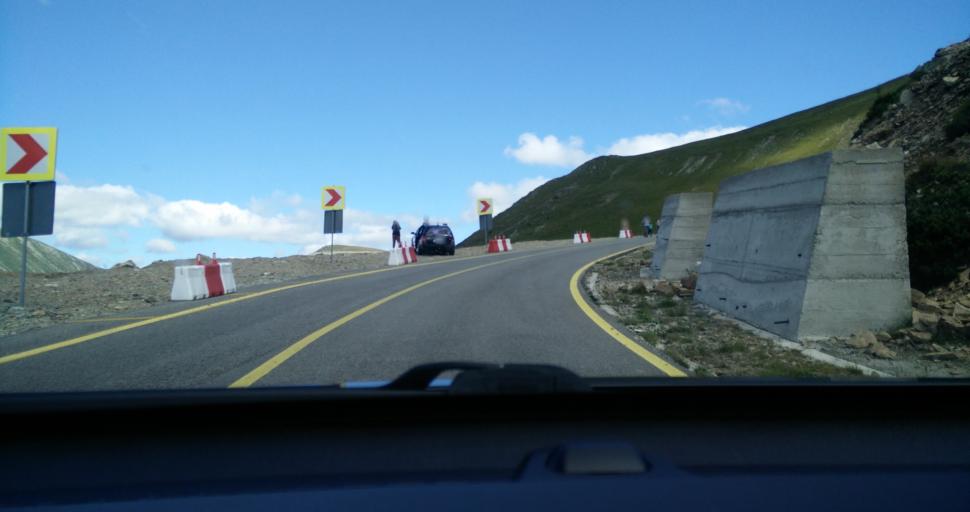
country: RO
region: Gorj
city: Novaci-Straini
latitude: 45.3237
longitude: 23.6823
